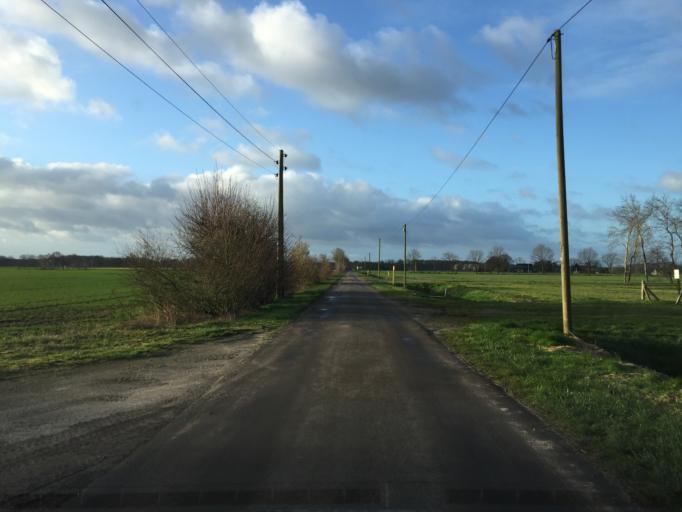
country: DE
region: Lower Saxony
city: Borstel
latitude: 52.6114
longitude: 8.9536
